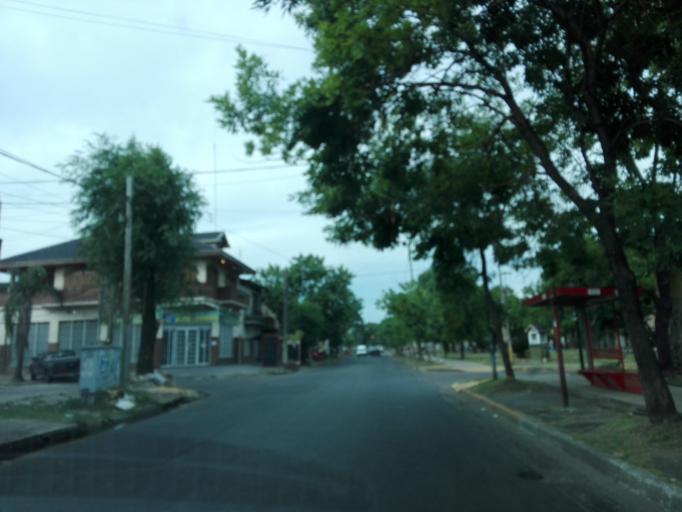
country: AR
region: Buenos Aires
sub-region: Partido de Lanus
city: Lanus
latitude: -34.7032
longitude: -58.3666
